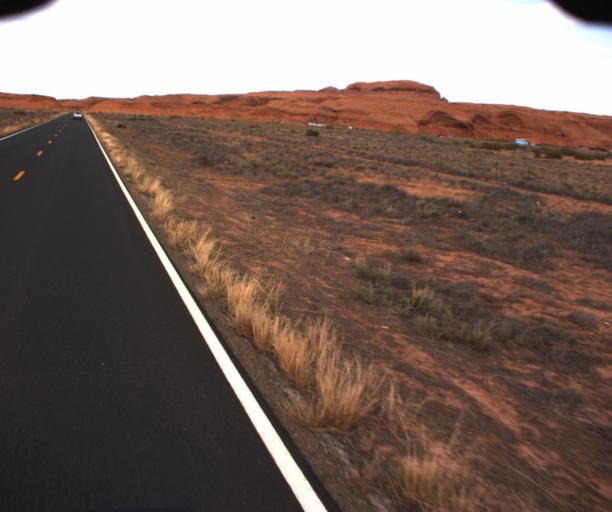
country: US
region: Arizona
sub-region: Apache County
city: Many Farms
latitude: 36.7575
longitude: -109.6478
